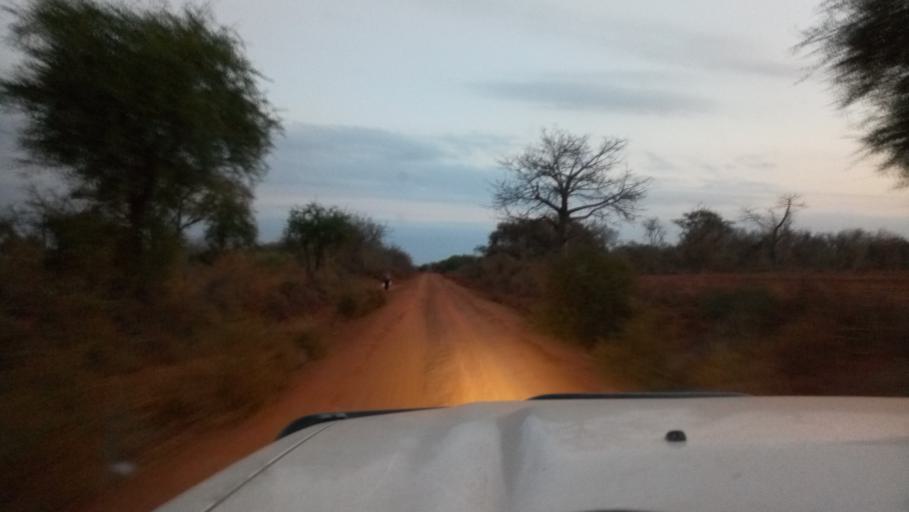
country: KE
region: Kitui
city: Kitui
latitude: -1.7731
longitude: 38.1865
